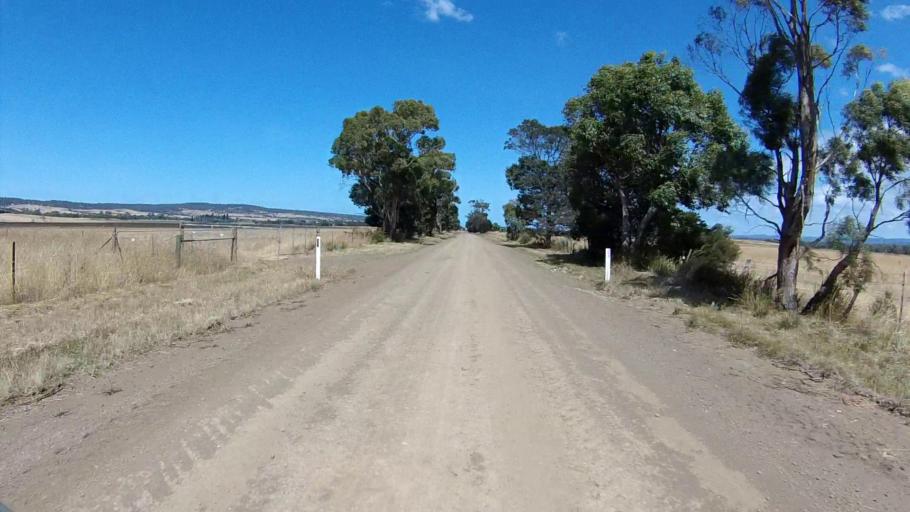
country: AU
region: Tasmania
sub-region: Break O'Day
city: St Helens
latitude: -41.9874
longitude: 148.0663
